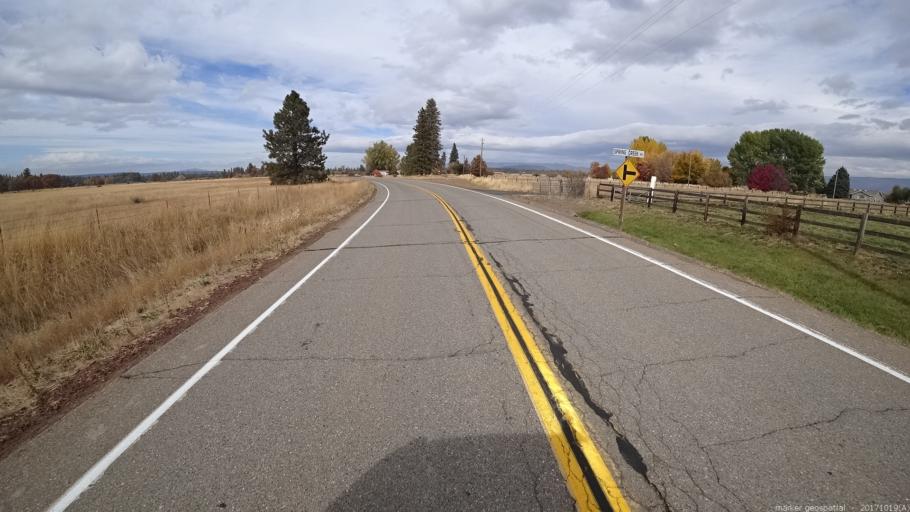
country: US
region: California
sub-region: Shasta County
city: Burney
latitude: 41.0918
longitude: -121.5144
